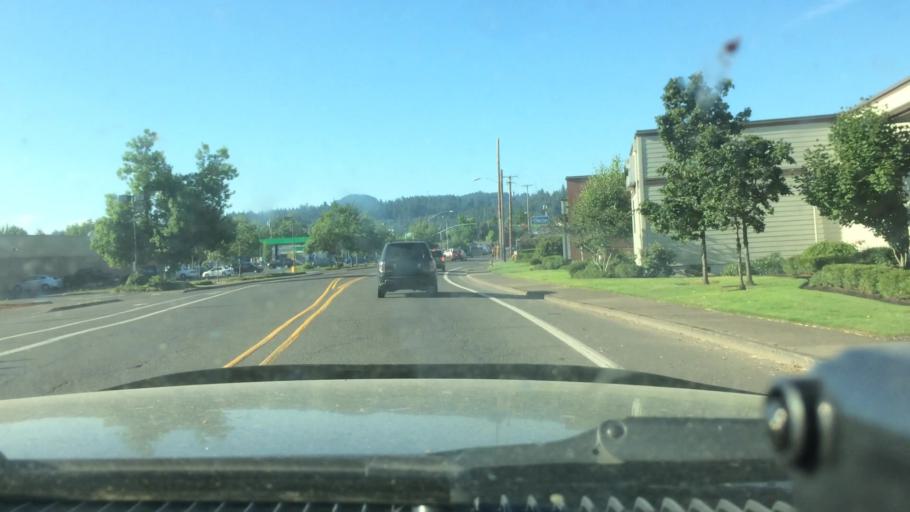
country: US
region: Oregon
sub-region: Lane County
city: Eugene
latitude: 44.0422
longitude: -123.1181
